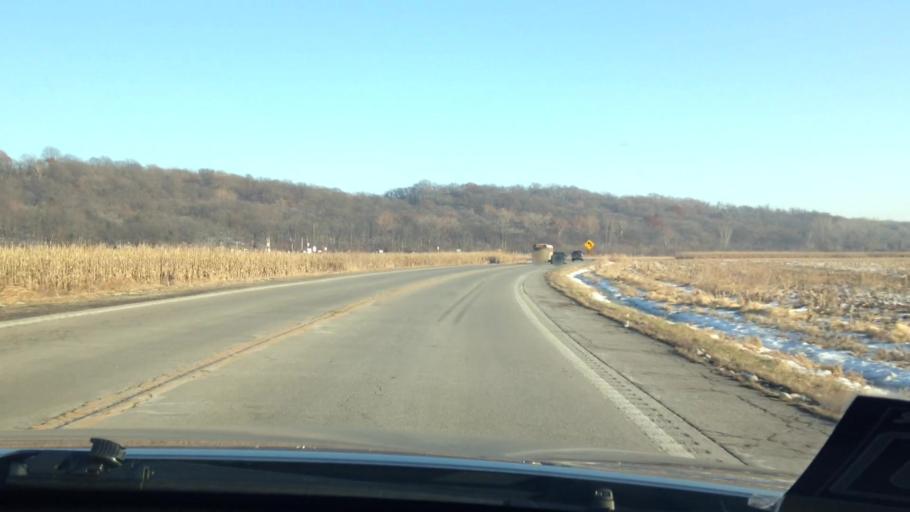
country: US
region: Kansas
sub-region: Leavenworth County
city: Leavenworth
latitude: 39.3238
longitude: -94.8604
